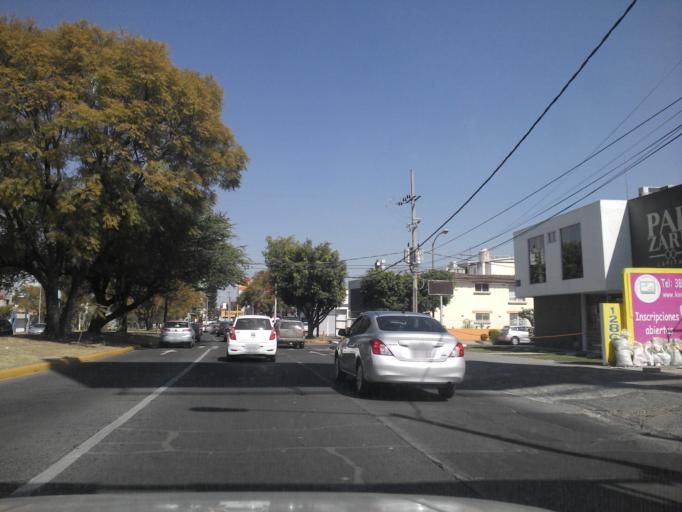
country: MX
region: Jalisco
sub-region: Zapopan
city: Zapopan
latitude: 20.6998
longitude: -103.3681
